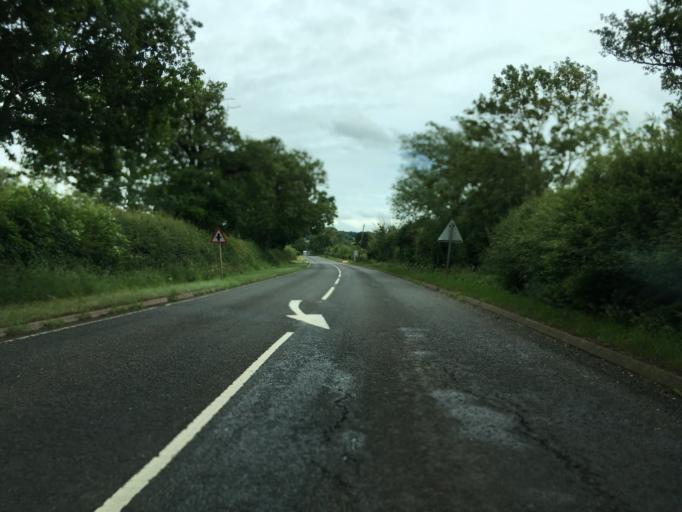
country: GB
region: England
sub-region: Northamptonshire
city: Daventry
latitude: 52.2512
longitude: -1.2468
